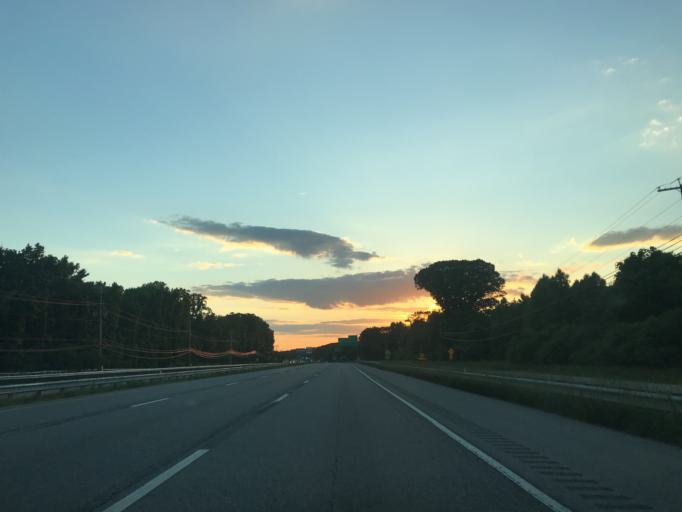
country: US
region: Maryland
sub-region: Anne Arundel County
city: Cape Saint Claire
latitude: 39.0240
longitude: -76.4297
